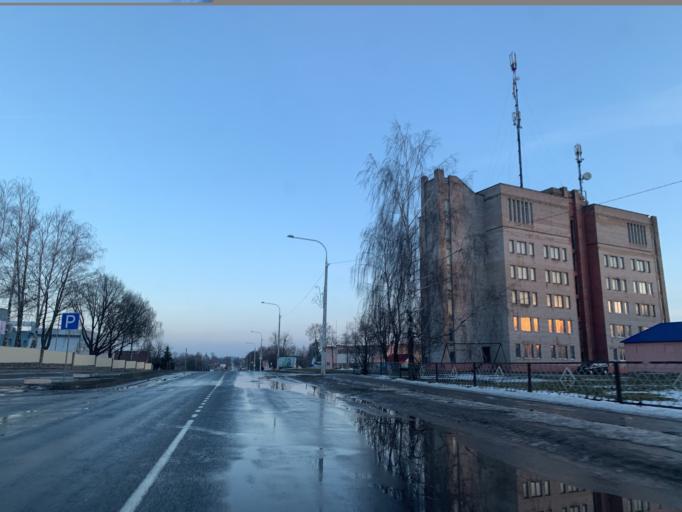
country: BY
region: Minsk
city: Nyasvizh
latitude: 53.2303
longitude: 26.6583
